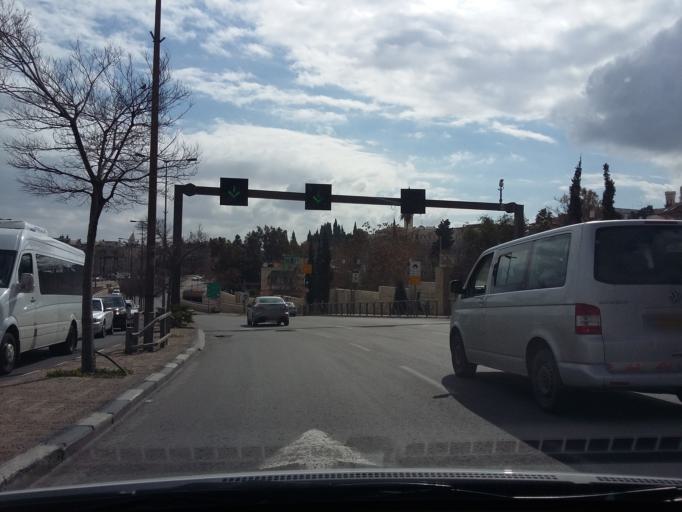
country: PS
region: West Bank
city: East Jerusalem
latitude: 31.7831
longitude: 35.2272
